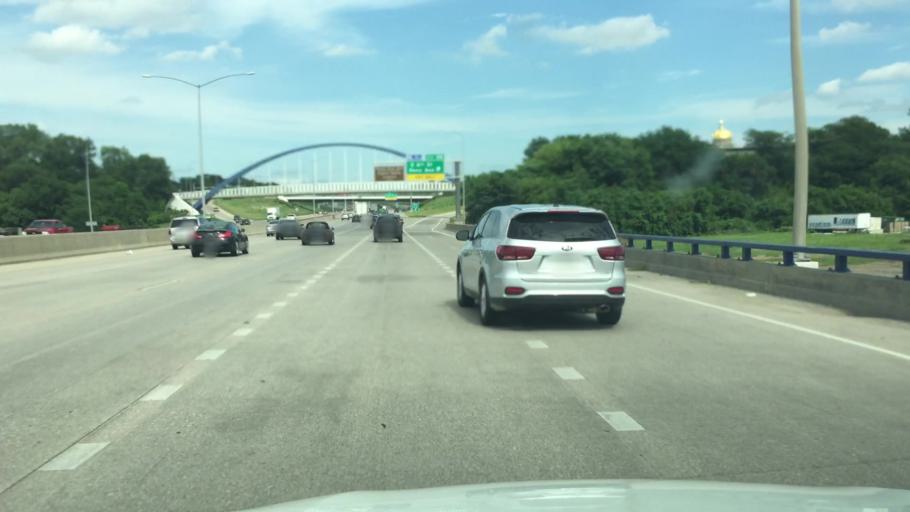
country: US
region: Iowa
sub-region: Polk County
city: Des Moines
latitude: 41.5954
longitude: -93.6163
